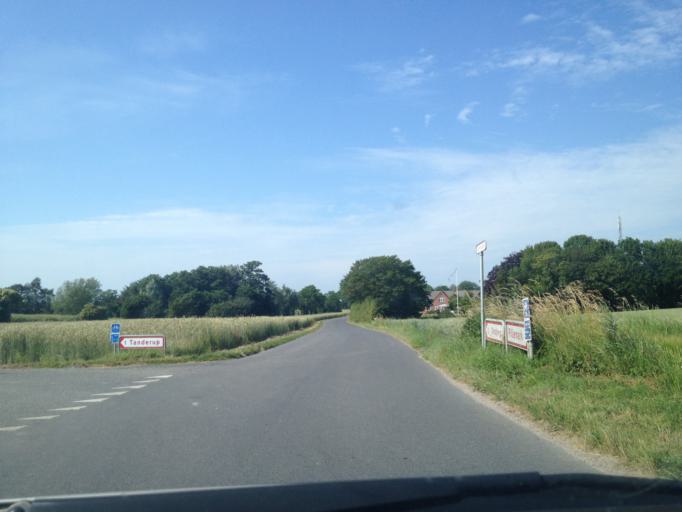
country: DK
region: Central Jutland
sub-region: Samso Kommune
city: Tranebjerg
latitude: 55.8309
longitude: 10.5600
